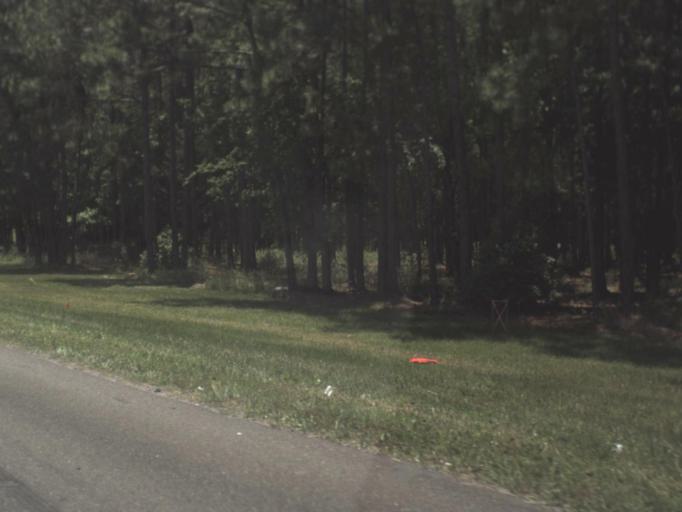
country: US
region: Florida
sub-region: Nassau County
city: Nassau Village-Ratliff
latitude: 30.4414
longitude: -81.7227
